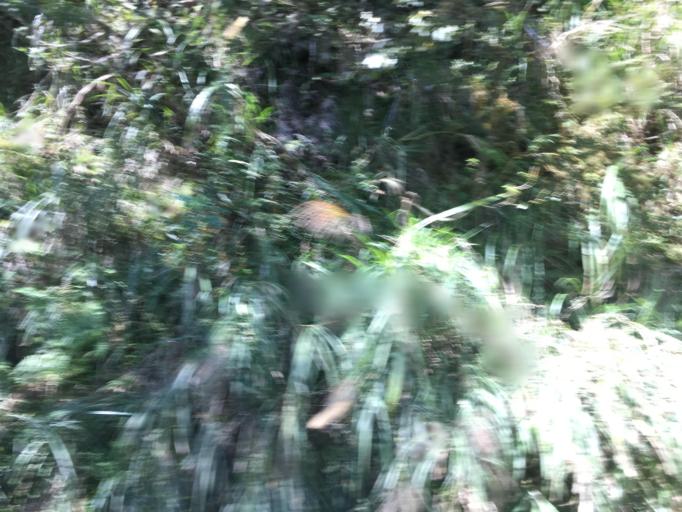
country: TW
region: Taiwan
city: Daxi
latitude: 24.6081
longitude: 121.4592
